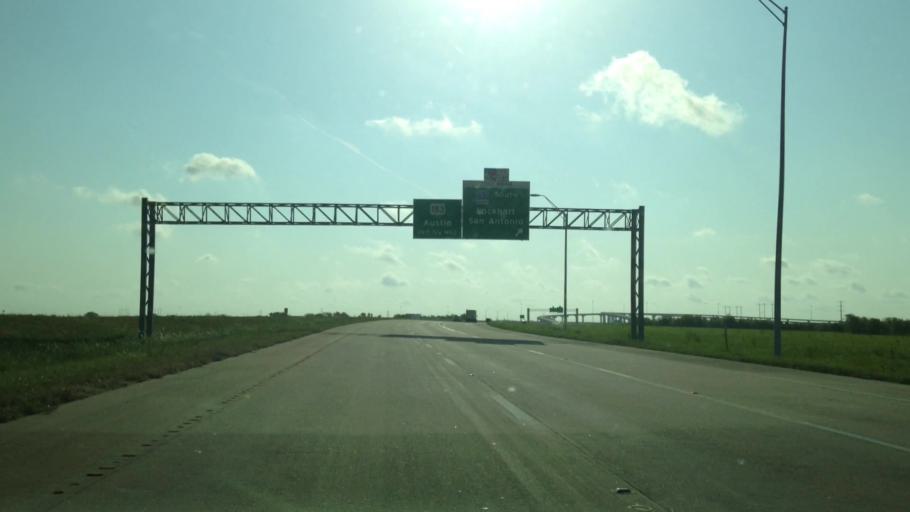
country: US
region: Texas
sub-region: Travis County
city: Onion Creek
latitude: 30.0819
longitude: -97.7131
